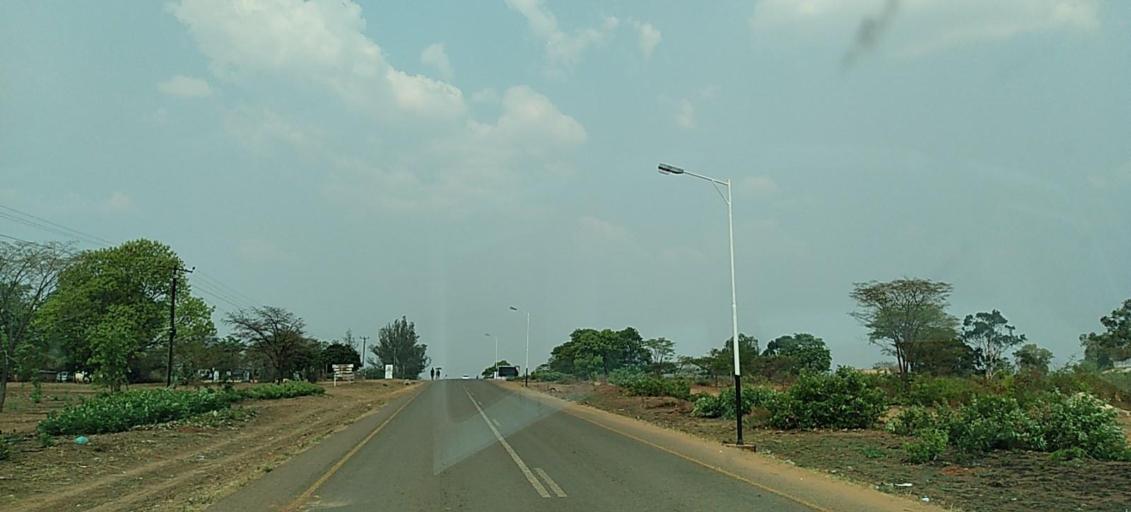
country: ZM
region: North-Western
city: Kabompo
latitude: -13.5926
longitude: 24.2062
